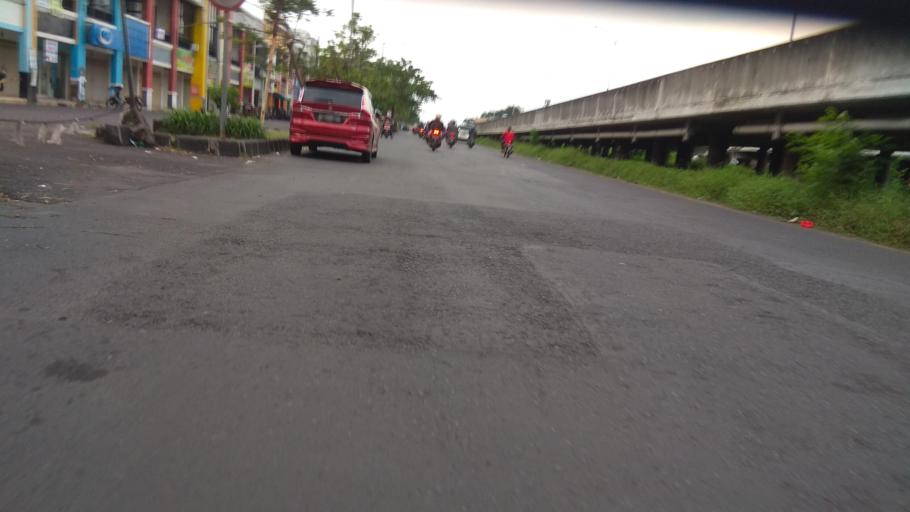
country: ID
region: East Java
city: Wadungasri
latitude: -7.3431
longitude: 112.7701
